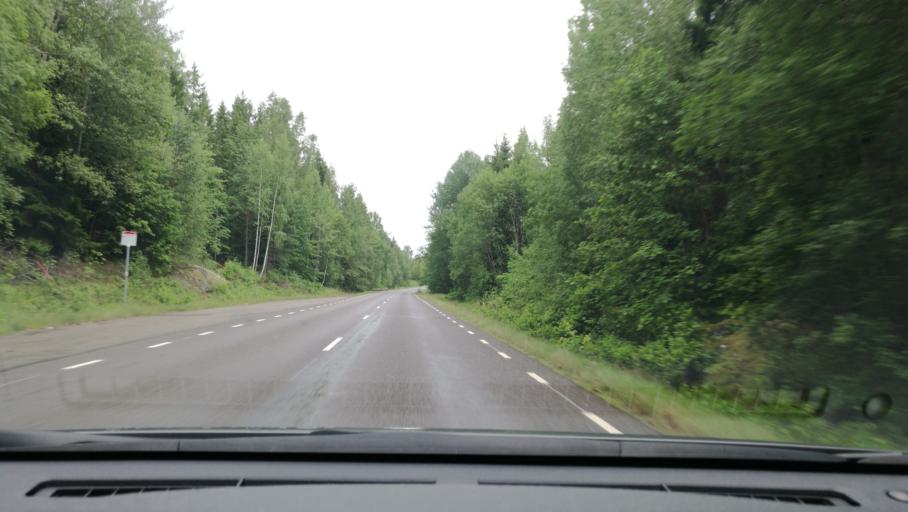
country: SE
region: OEstergoetland
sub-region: Norrkopings Kommun
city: Svartinge
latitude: 58.7904
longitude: 15.9593
